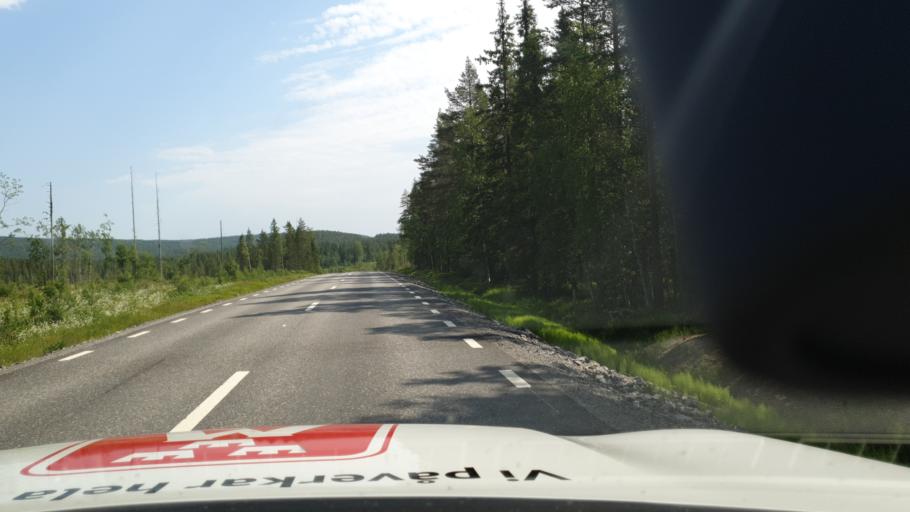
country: SE
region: Vaesterbotten
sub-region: Umea Kommun
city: Ersmark
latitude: 64.2583
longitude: 20.1956
